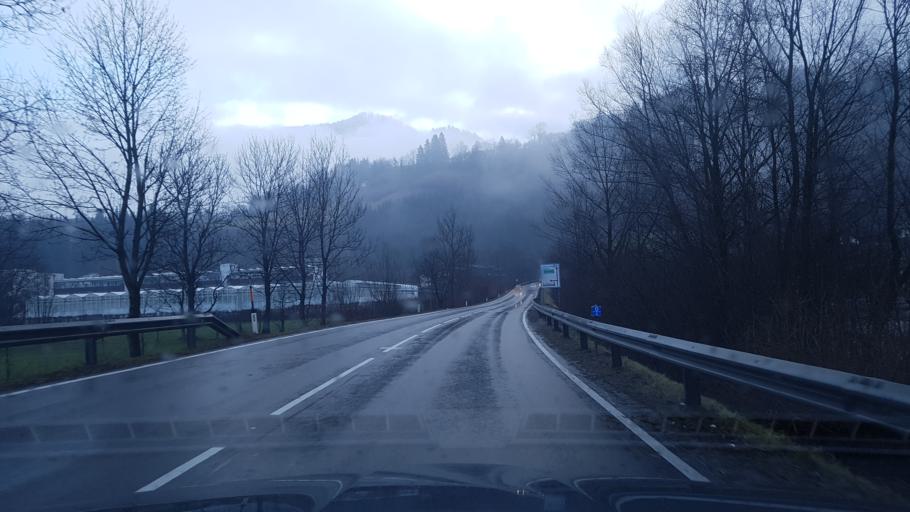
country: AT
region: Salzburg
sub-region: Politischer Bezirk Sankt Johann im Pongau
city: Sankt Johann im Pongau
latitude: 47.3401
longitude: 13.1946
